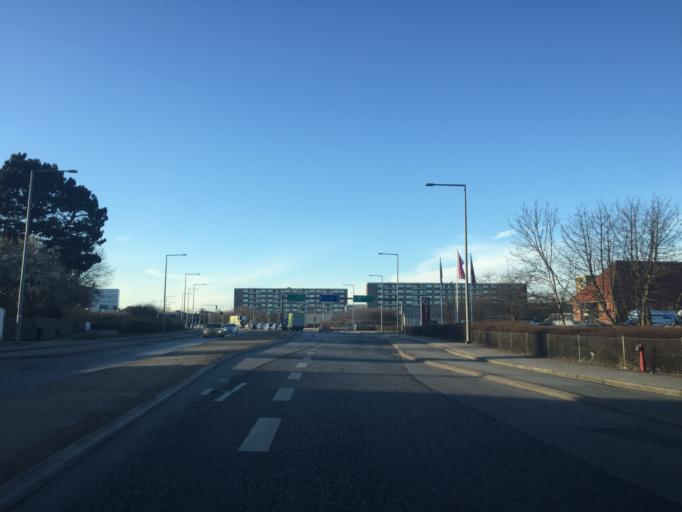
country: DK
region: Capital Region
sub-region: Tarnby Kommune
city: Tarnby
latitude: 55.6279
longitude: 12.6039
